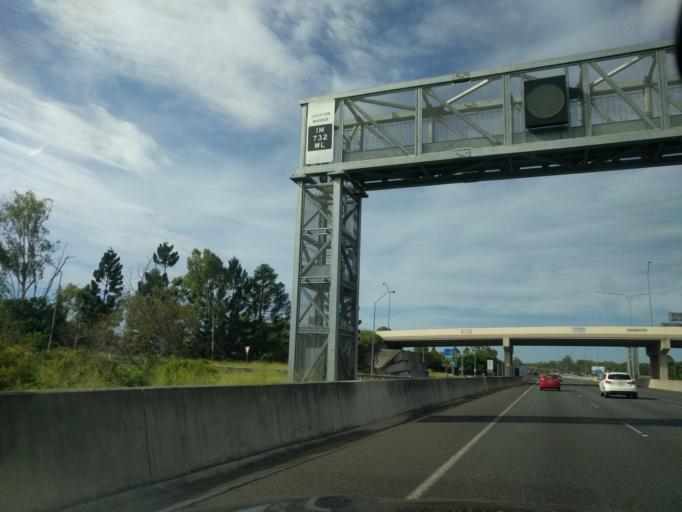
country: AU
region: Queensland
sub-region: Brisbane
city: Wacol
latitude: -27.5881
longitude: 152.9274
